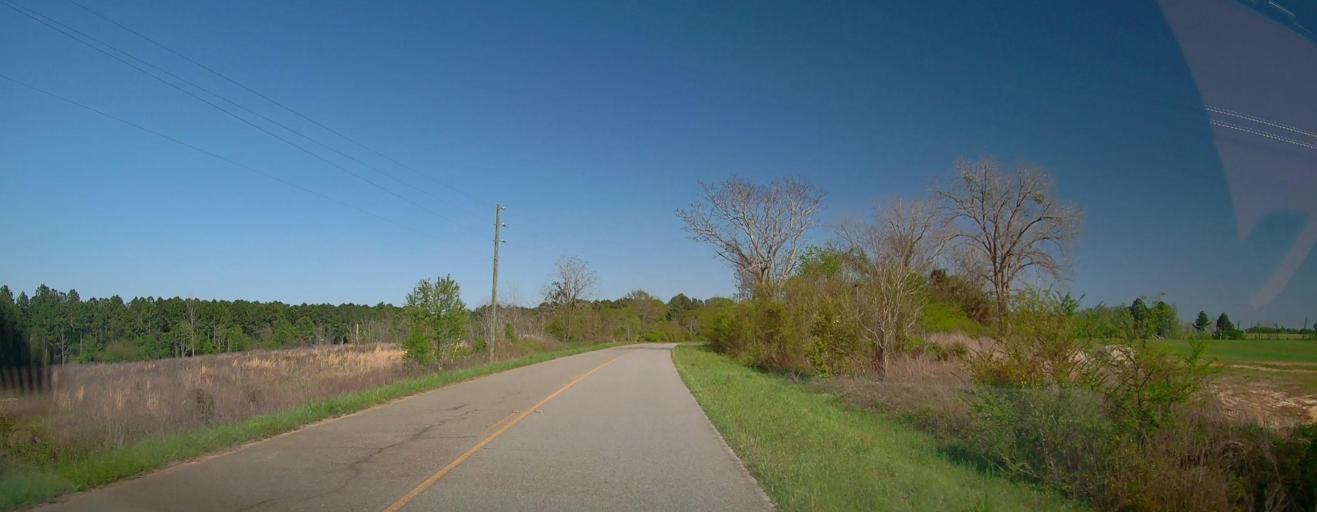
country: US
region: Georgia
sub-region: Pulaski County
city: Hawkinsville
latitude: 32.2450
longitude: -83.5715
